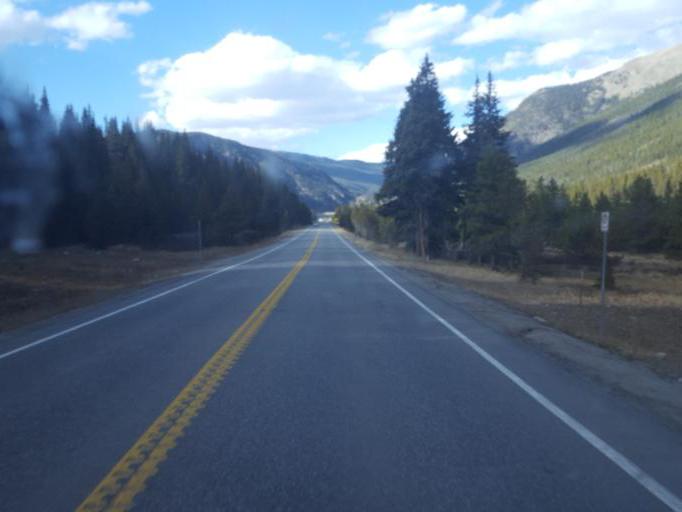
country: US
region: Colorado
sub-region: Summit County
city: Frisco
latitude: 39.4862
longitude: -106.1342
